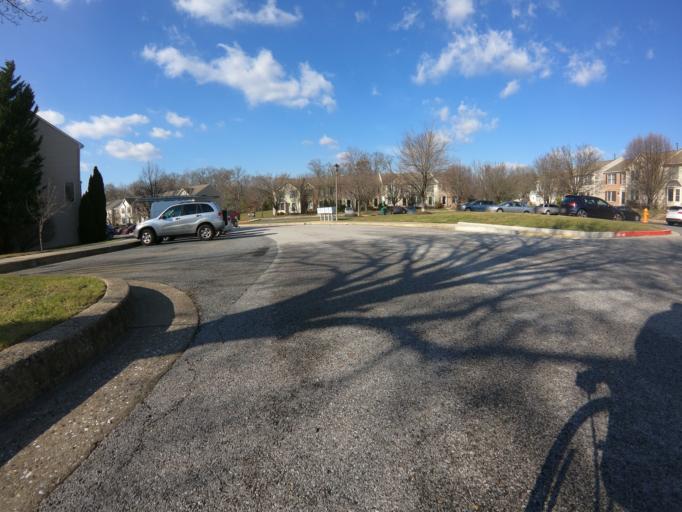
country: US
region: Maryland
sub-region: Howard County
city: Ilchester
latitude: 39.2138
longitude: -76.7856
